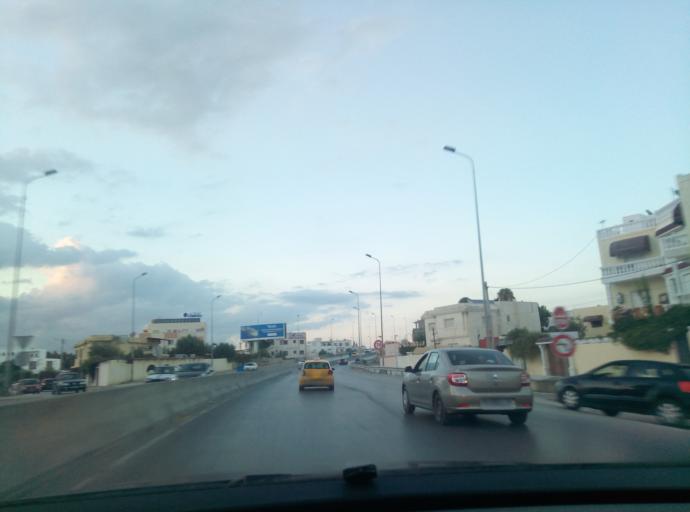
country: TN
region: Manouba
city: Manouba
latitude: 36.8076
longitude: 10.1187
